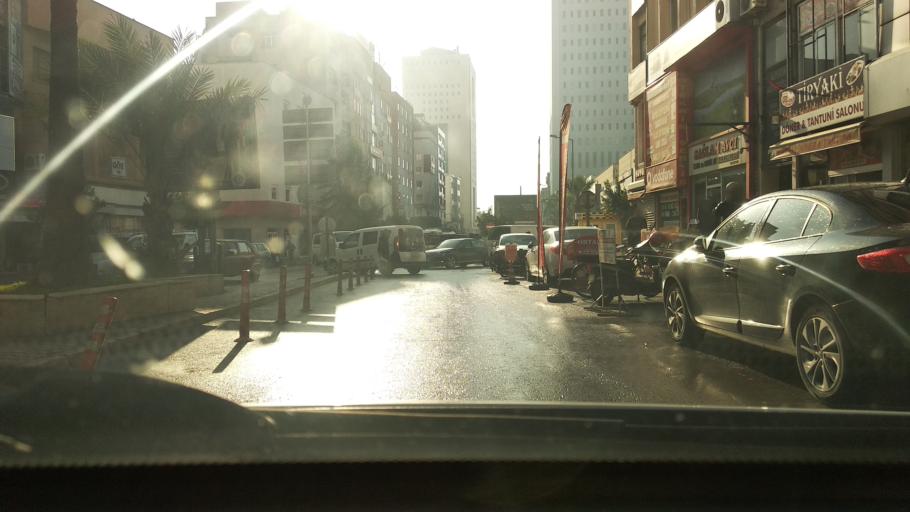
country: TR
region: Mersin
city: Mercin
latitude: 36.8052
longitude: 34.6231
